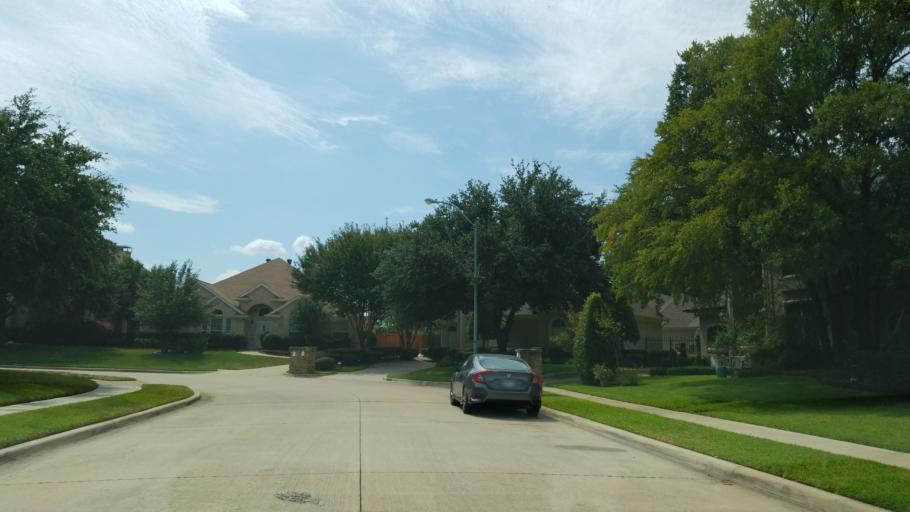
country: US
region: Texas
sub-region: Tarrant County
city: Grapevine
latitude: 32.8966
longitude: -97.1028
